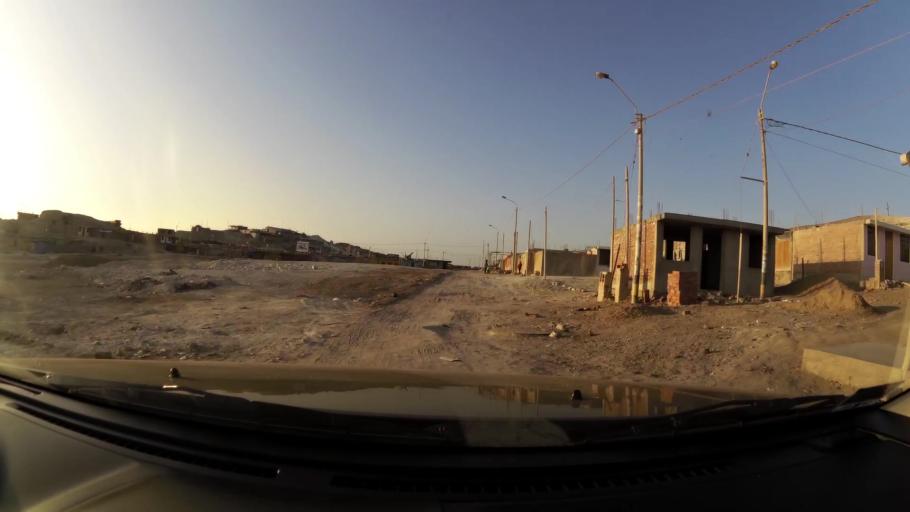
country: PE
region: Ica
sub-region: Provincia de Pisco
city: Villa Tupac Amaru
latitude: -13.6999
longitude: -76.1574
